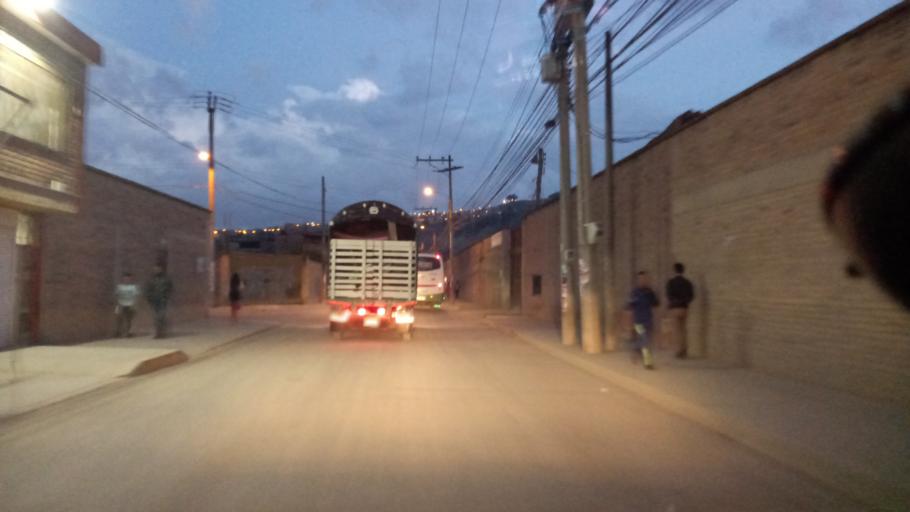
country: CO
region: Cundinamarca
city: Soacha
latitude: 4.5683
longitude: -74.2319
